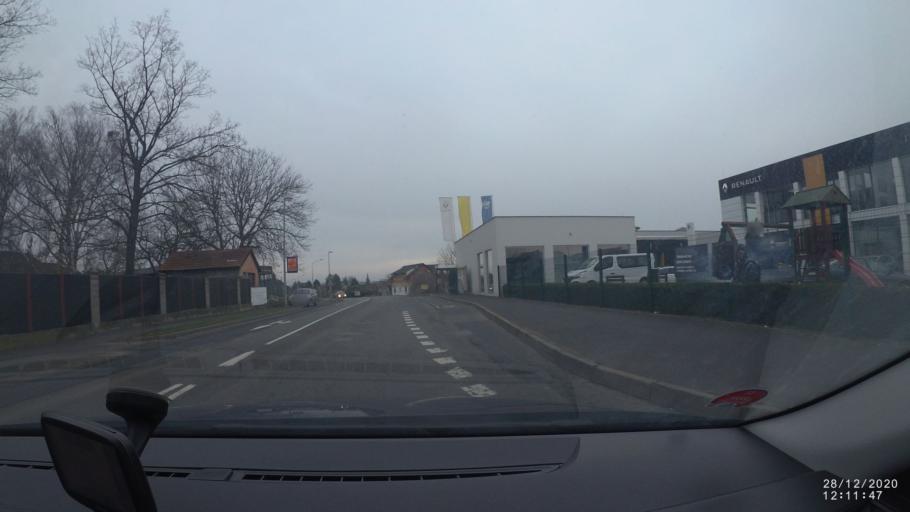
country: CZ
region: Central Bohemia
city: Brandys nad Labem-Stara Boleslav
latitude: 50.1744
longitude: 14.6490
